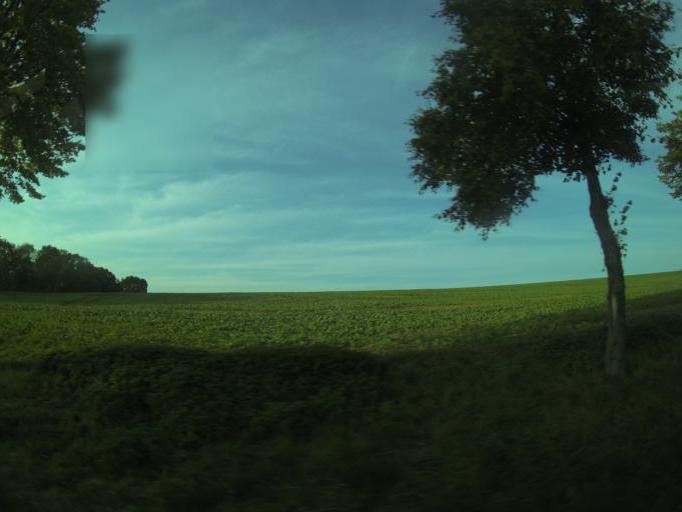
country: DE
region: Thuringia
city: Altkirchen
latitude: 50.9341
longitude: 12.3778
